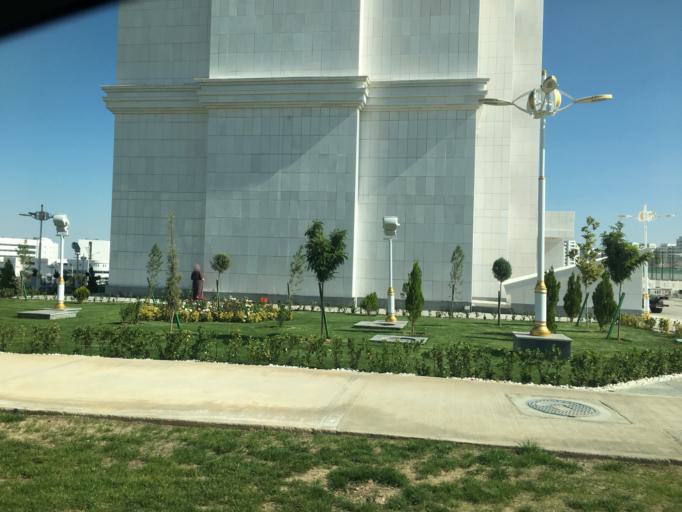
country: TM
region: Ahal
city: Ashgabat
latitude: 37.9392
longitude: 58.3554
